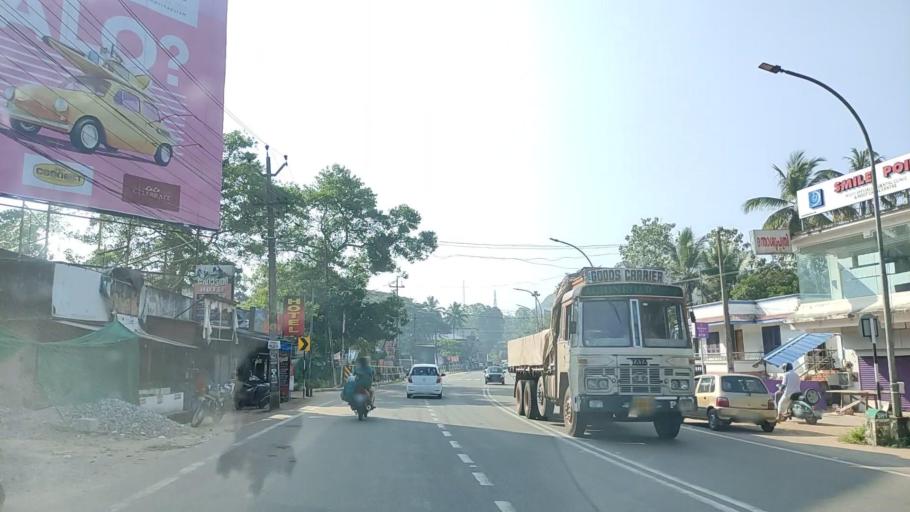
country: IN
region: Kerala
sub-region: Kollam
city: Punalur
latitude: 8.8751
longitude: 76.8694
